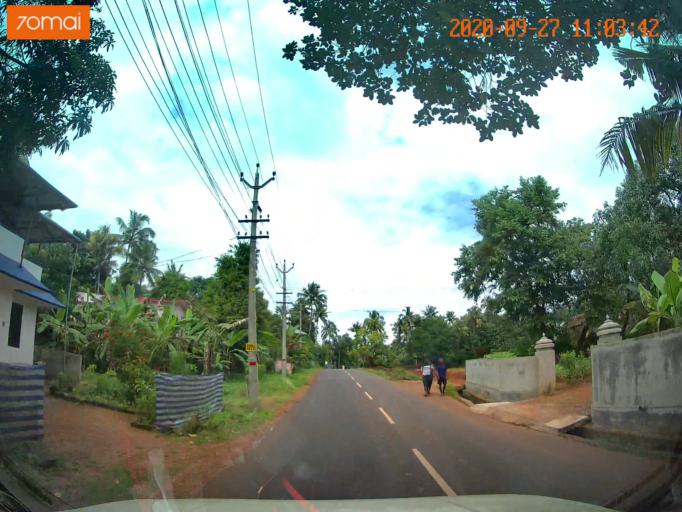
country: IN
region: Kerala
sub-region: Thrissur District
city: Irinjalakuda
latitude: 10.4220
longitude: 76.2545
